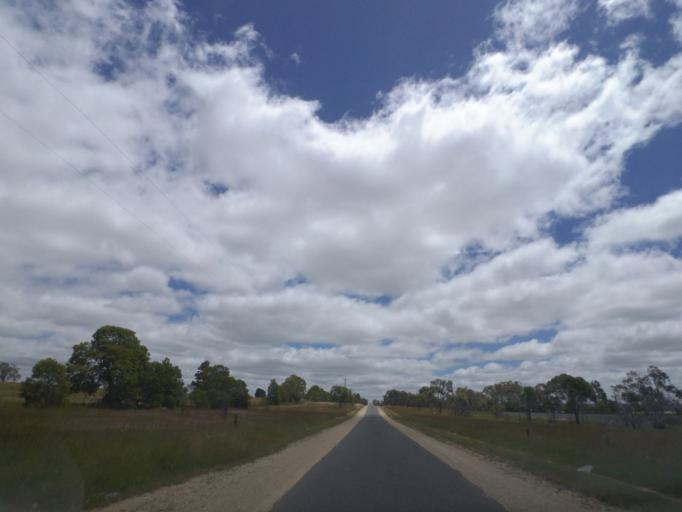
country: AU
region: Victoria
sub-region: Moorabool
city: Bacchus Marsh
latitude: -37.6293
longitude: 144.2661
